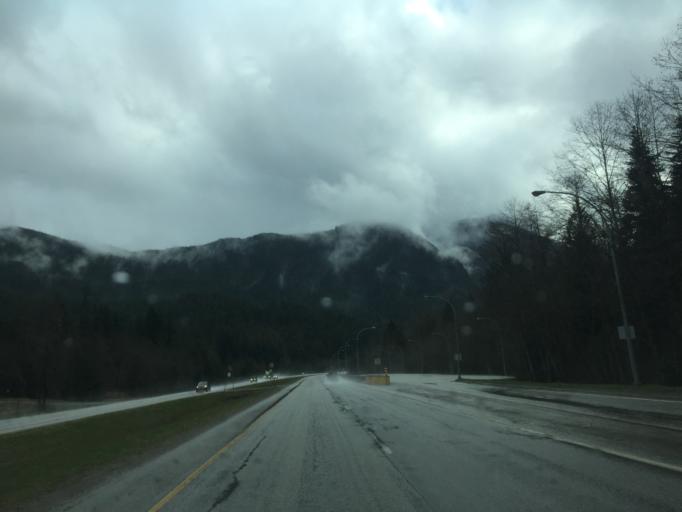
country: CA
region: British Columbia
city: Hope
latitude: 49.4680
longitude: -121.2547
